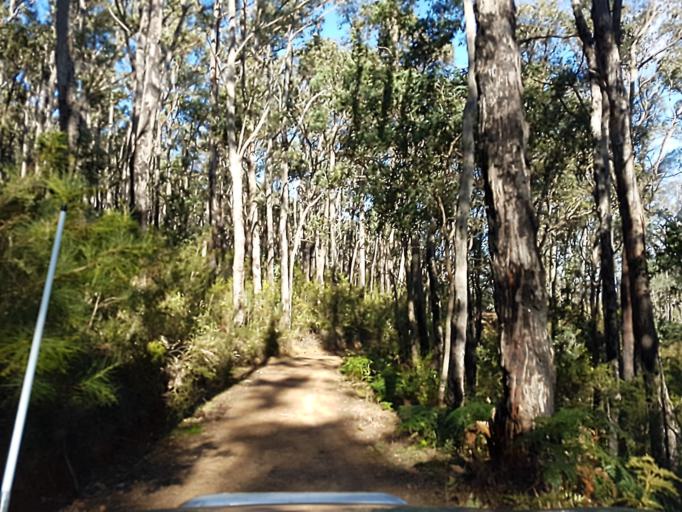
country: AU
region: Victoria
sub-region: Yarra Ranges
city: Healesville
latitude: -37.5726
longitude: 145.4823
